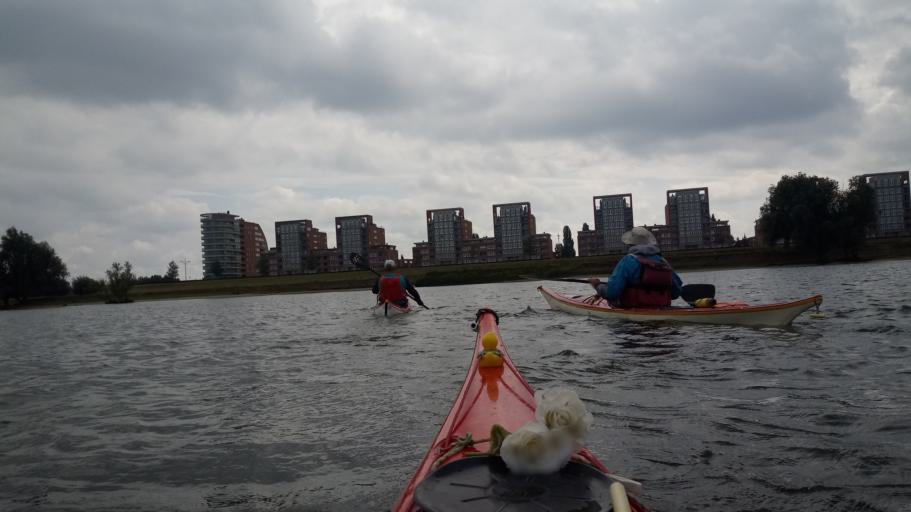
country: NL
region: Gelderland
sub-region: Gemeente Maasdriel
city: Hedel
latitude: 51.7404
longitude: 5.2791
